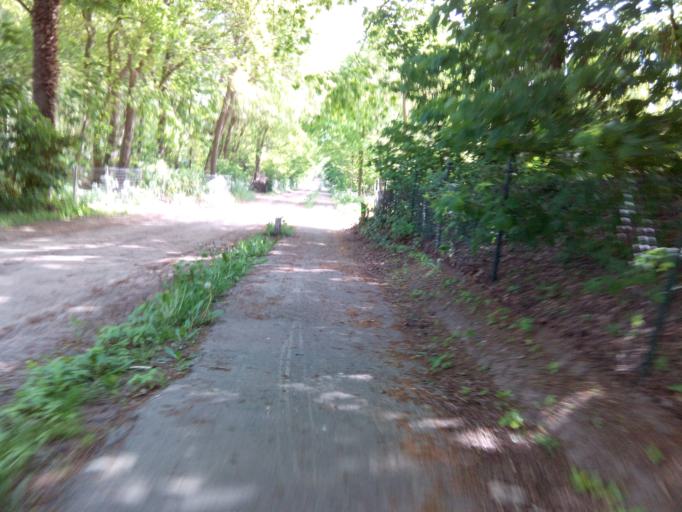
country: NL
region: Gelderland
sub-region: Gemeente Ede
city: Lunteren
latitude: 52.0715
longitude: 5.6485
